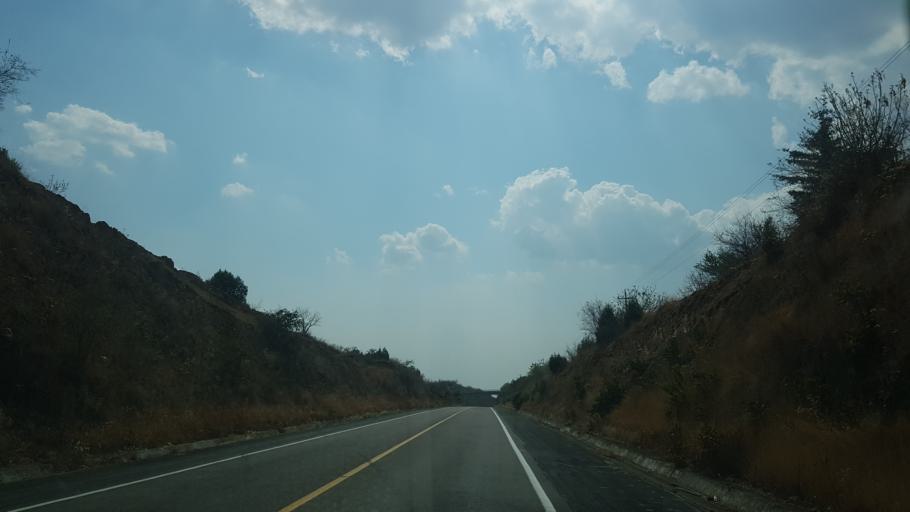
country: MX
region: Puebla
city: San Juan Amecac
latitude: 18.8160
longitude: -98.6670
